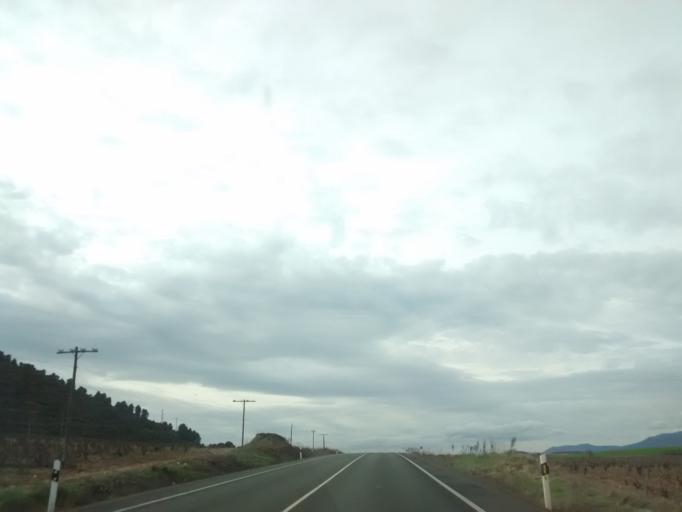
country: ES
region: La Rioja
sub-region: Provincia de La Rioja
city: Torremontalbo
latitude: 42.5046
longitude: -2.6911
